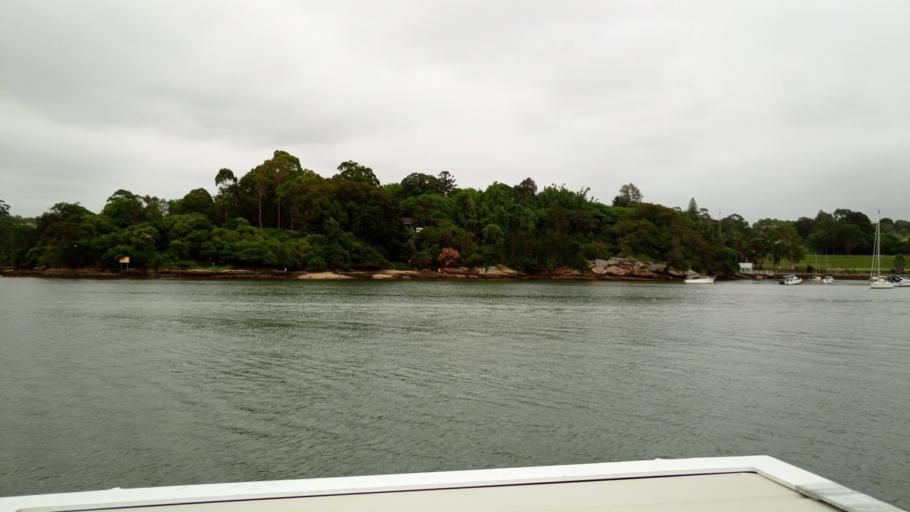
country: AU
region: New South Wales
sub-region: Hunters Hill
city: Gladesville
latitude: -33.8434
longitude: 151.1295
